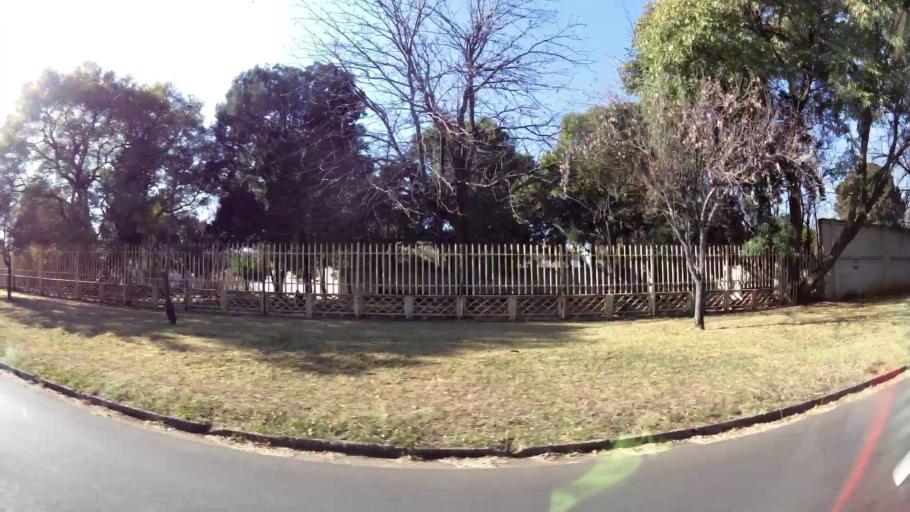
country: ZA
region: Gauteng
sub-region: City of Johannesburg Metropolitan Municipality
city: Modderfontein
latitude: -26.1596
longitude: 28.1360
